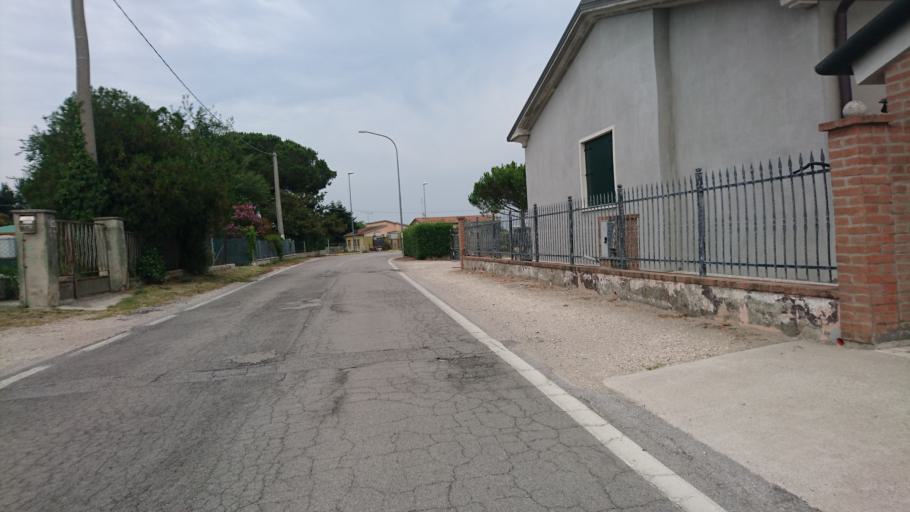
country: IT
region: Veneto
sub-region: Provincia di Rovigo
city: Rosolina
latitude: 45.0984
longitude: 12.2462
